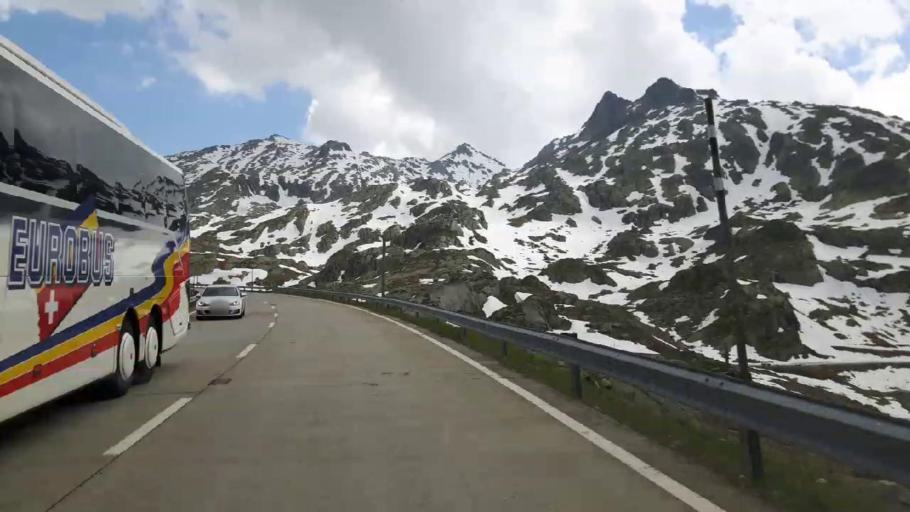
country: CH
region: Ticino
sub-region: Leventina District
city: Airolo
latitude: 46.5626
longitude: 8.5591
